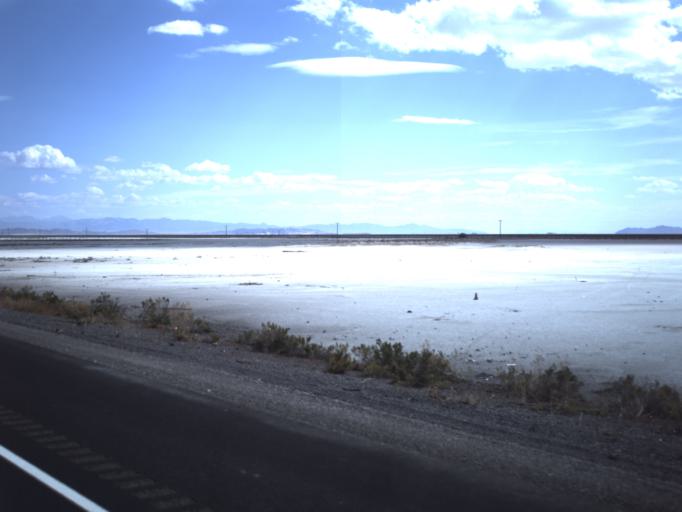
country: US
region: Utah
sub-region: Tooele County
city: Wendover
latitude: 40.7308
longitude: -113.4972
